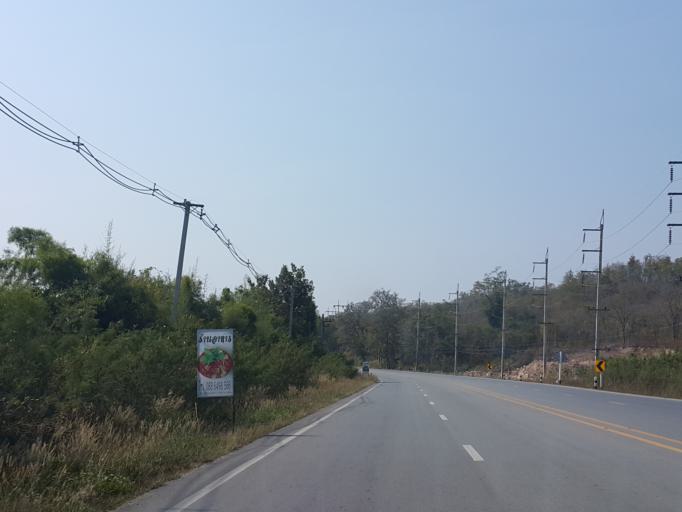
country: TH
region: Chiang Mai
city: Chom Thong
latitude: 18.3300
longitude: 98.6690
